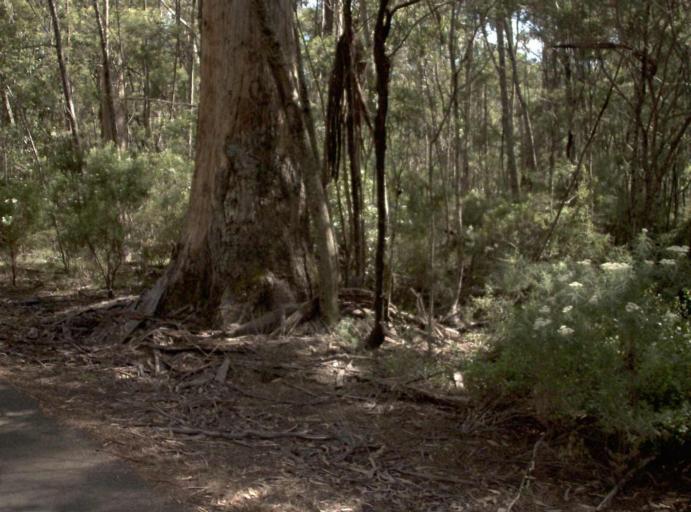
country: AU
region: Victoria
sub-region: East Gippsland
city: Lakes Entrance
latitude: -37.4336
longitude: 148.1293
